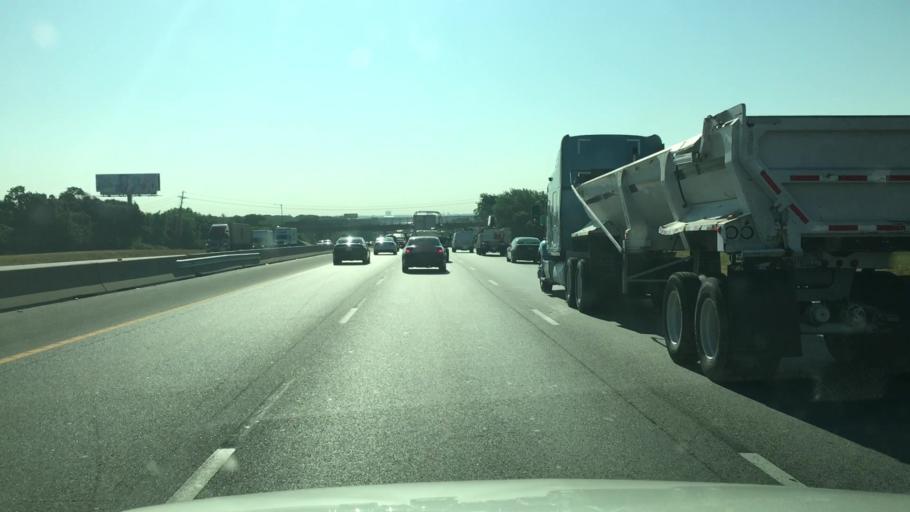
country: US
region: Texas
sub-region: Tarrant County
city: Richland Hills
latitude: 32.7596
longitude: -97.2005
